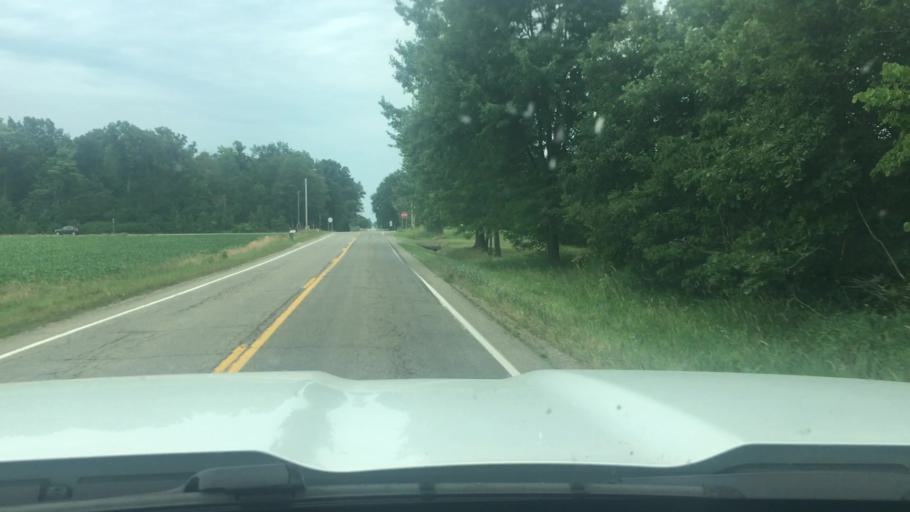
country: US
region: Michigan
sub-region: Clinton County
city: Saint Johns
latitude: 43.0023
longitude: -84.4840
